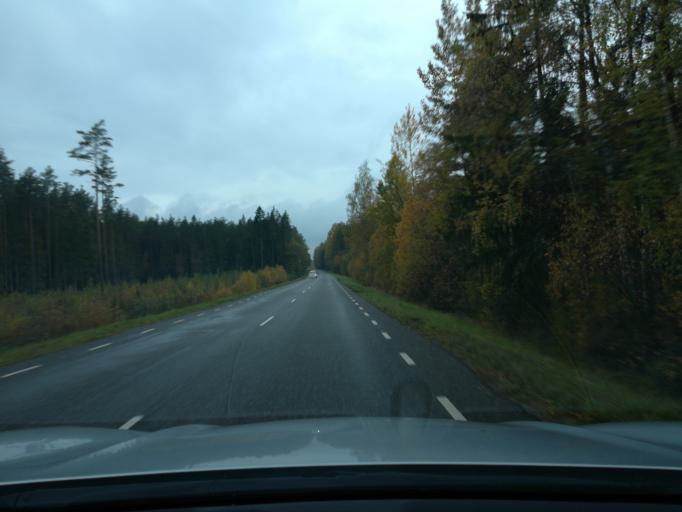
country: EE
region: Ida-Virumaa
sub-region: Johvi vald
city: Johvi
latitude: 59.0785
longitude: 27.3338
